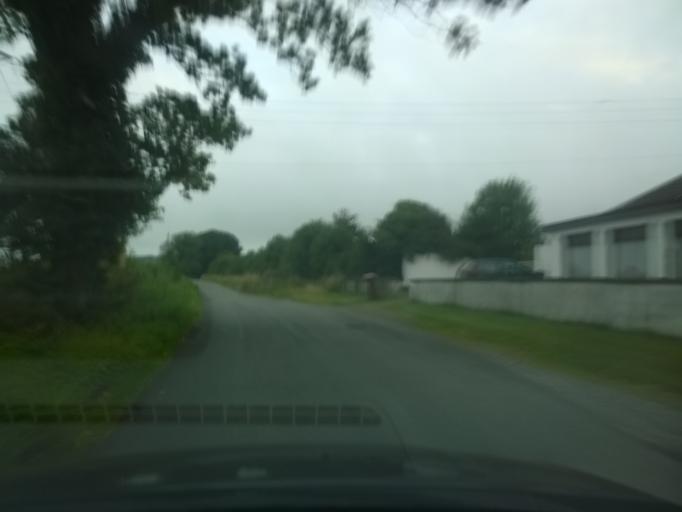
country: IE
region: Leinster
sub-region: Kildare
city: Kildare
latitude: 53.1731
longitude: -6.9310
